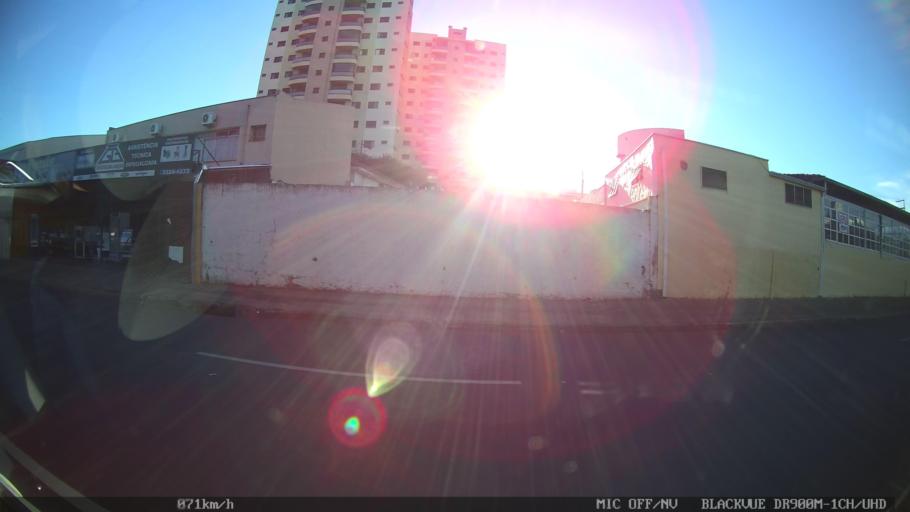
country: BR
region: Sao Paulo
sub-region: Araraquara
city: Araraquara
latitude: -21.7766
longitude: -48.1683
